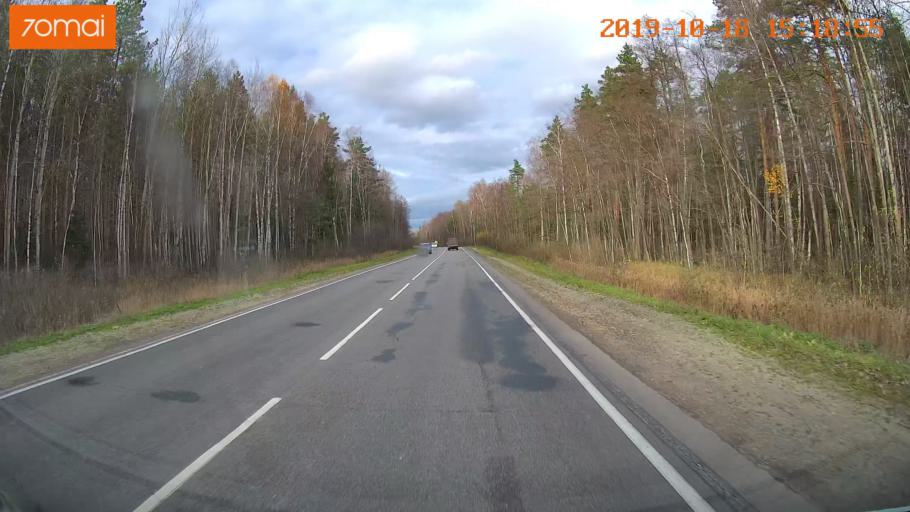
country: RU
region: Vladimir
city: Anopino
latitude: 55.6656
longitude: 40.7335
